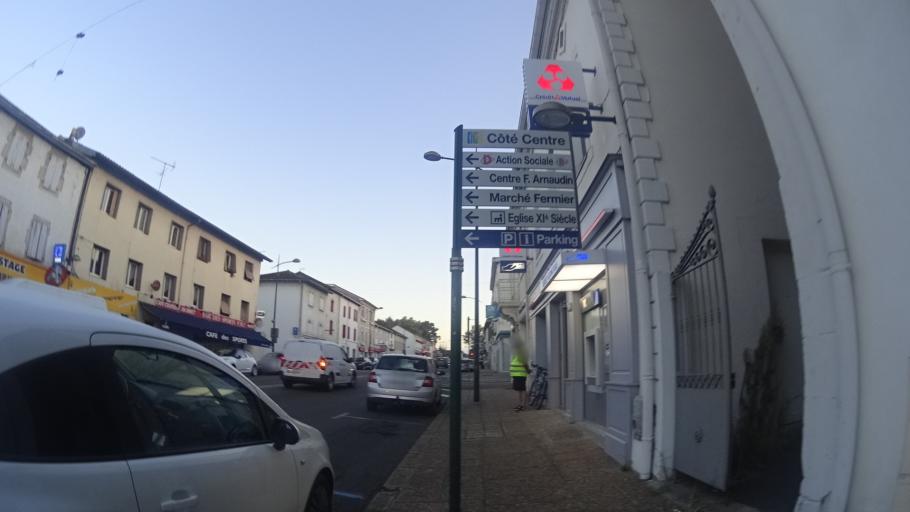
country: FR
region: Aquitaine
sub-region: Departement des Landes
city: Saint-Paul-les-Dax
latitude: 43.7219
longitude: -1.0518
